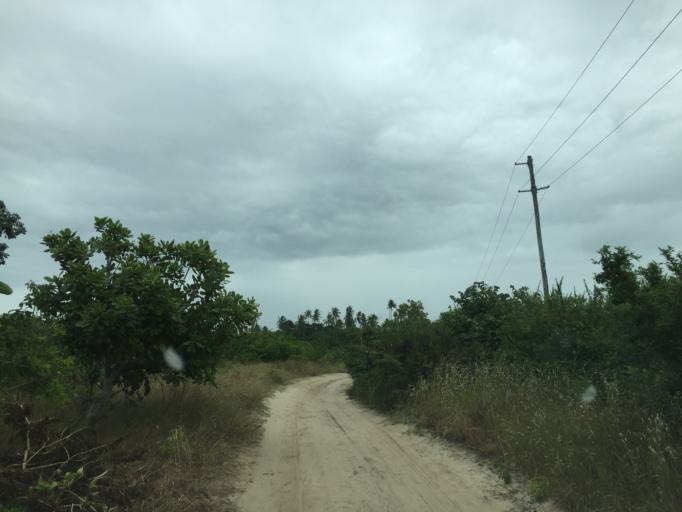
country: TZ
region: Pwani
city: Vikindu
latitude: -6.9408
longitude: 39.4900
